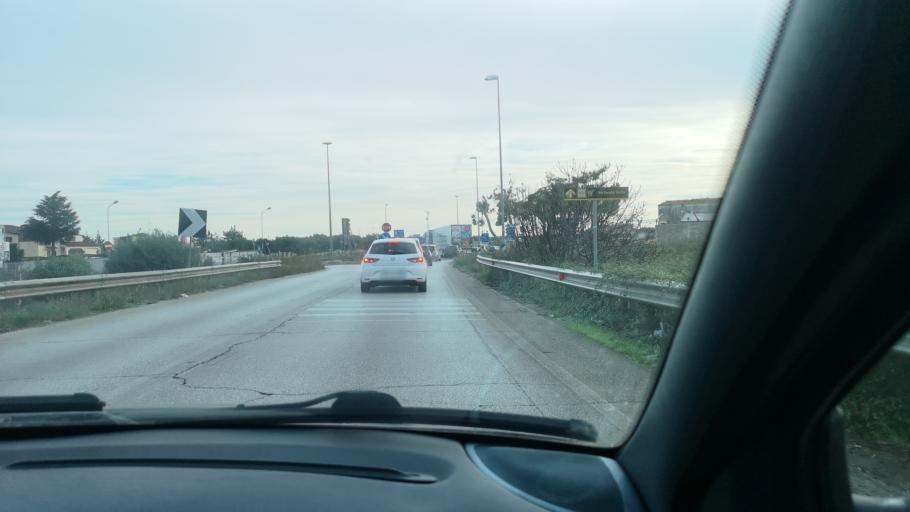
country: IT
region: Apulia
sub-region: Provincia di Bari
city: Sannicandro di Bari
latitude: 40.9914
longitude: 16.7990
